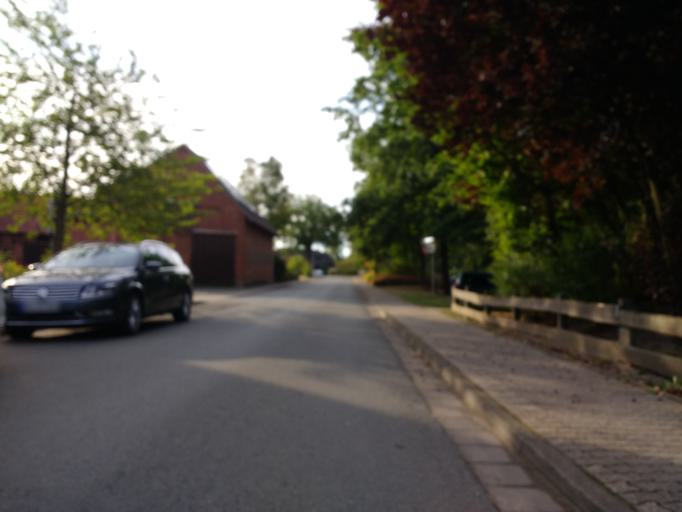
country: DE
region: Lower Saxony
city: Isenbuttel
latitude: 52.4375
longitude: 10.5788
